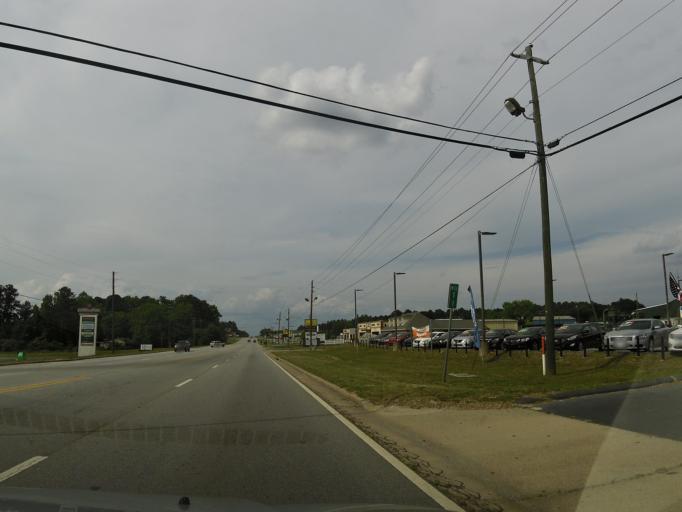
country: US
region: Georgia
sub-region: McDuffie County
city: Thomson
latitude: 33.4894
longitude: -82.5046
